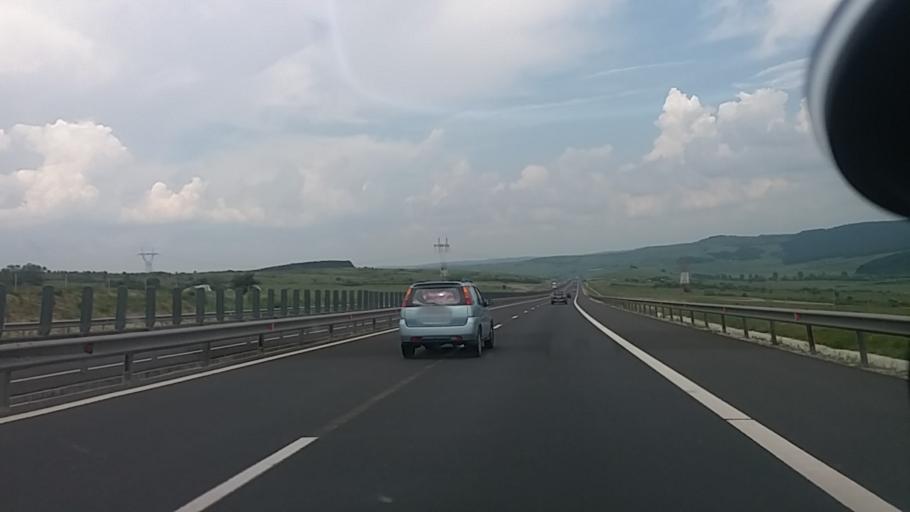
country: RO
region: Sibiu
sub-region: Comuna Apoldu de Jos
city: Apoldu de Jos
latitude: 45.8413
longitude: 23.8648
